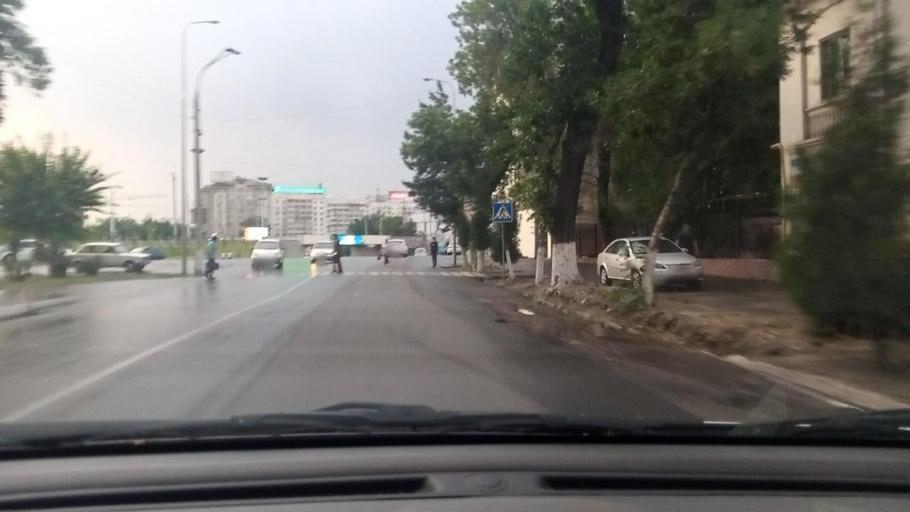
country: UZ
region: Toshkent Shahri
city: Tashkent
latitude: 41.2866
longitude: 69.2832
